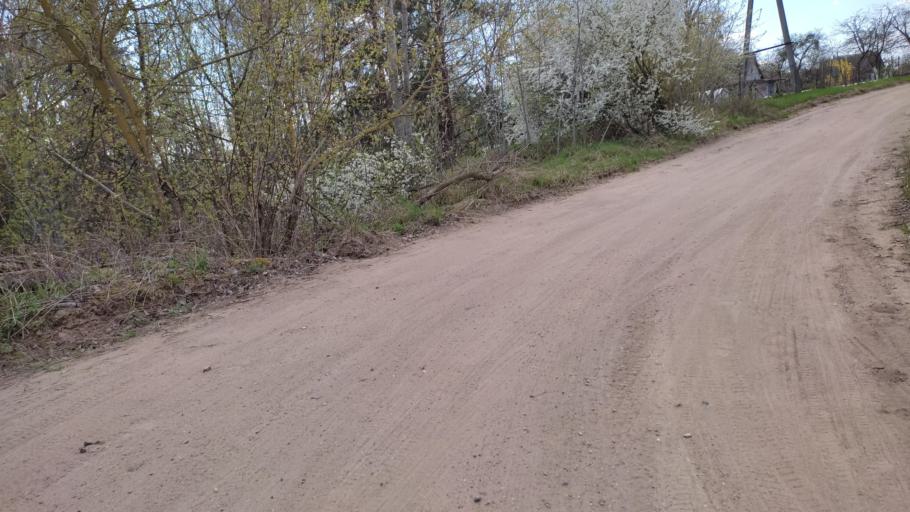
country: BY
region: Grodnenskaya
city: Hrodna
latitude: 53.6574
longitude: 23.8967
